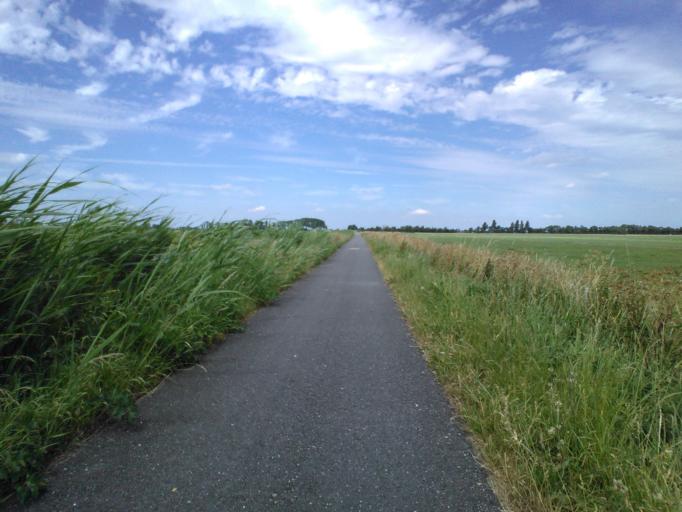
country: NL
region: South Holland
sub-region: Gemeente Giessenlanden
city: Giessenburg
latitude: 51.8709
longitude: 4.8780
